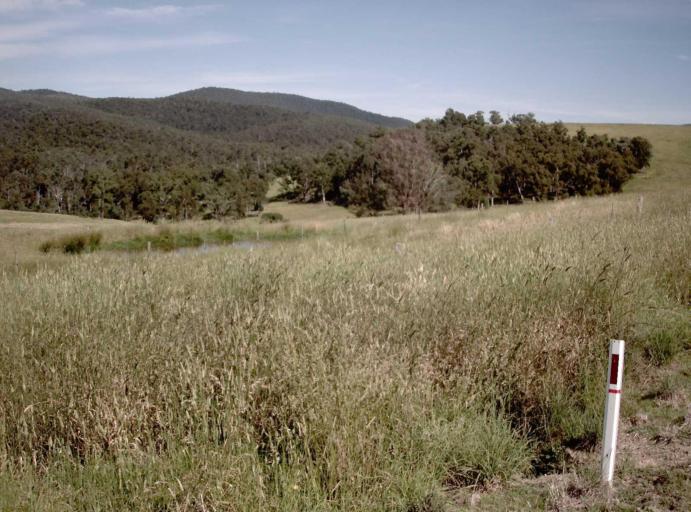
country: AU
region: Victoria
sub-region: East Gippsland
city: Lakes Entrance
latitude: -37.4993
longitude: 148.1327
